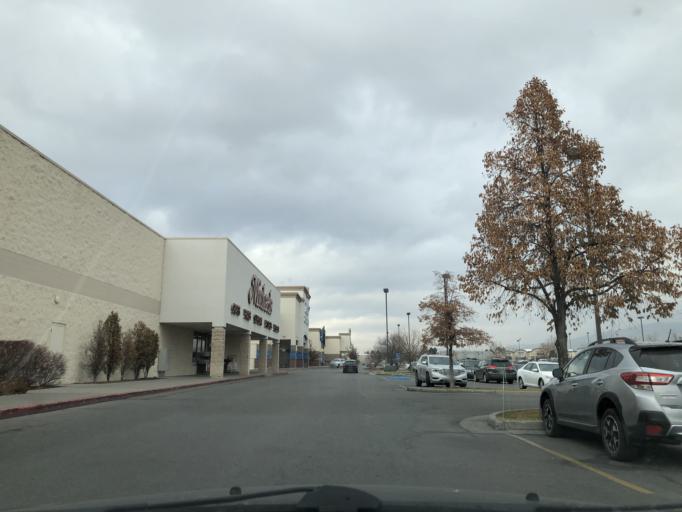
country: US
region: Utah
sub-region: Cache County
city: Logan
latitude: 41.7581
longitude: -111.8360
